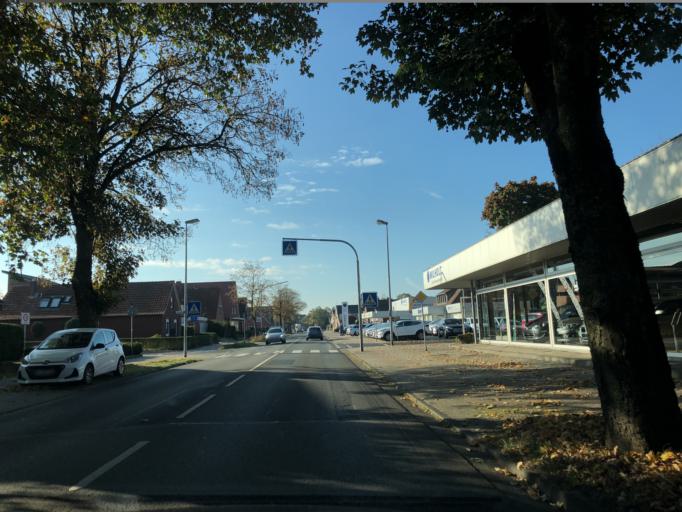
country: DE
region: Lower Saxony
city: Papenburg
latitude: 53.0743
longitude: 7.4250
